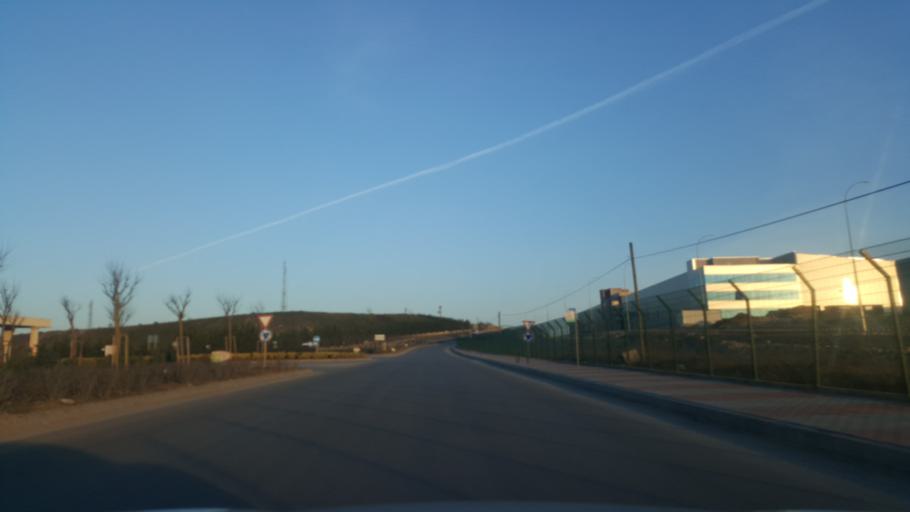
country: TR
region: Kocaeli
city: Tavsancil
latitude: 40.8186
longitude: 29.5635
